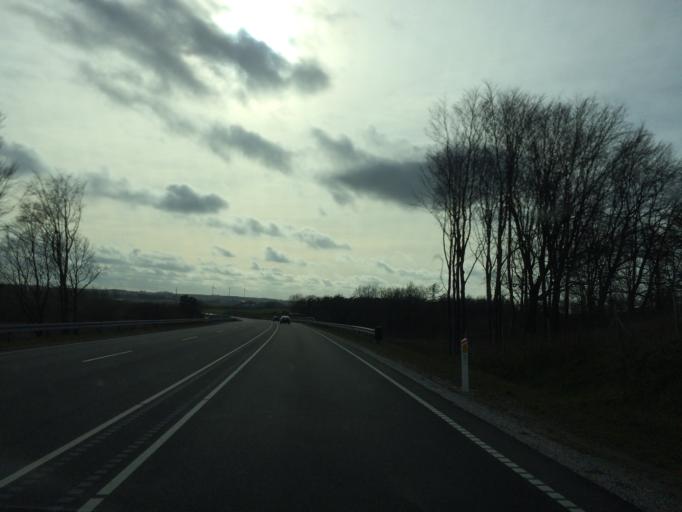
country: DK
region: Central Jutland
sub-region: Randers Kommune
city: Assentoft
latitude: 56.4303
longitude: 10.1251
